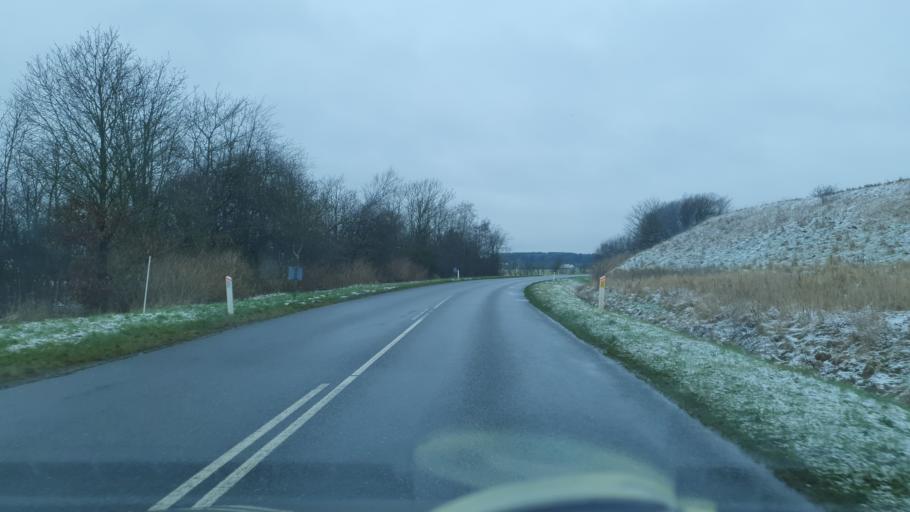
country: DK
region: North Denmark
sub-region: Jammerbugt Kommune
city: Brovst
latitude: 57.1015
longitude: 9.5052
